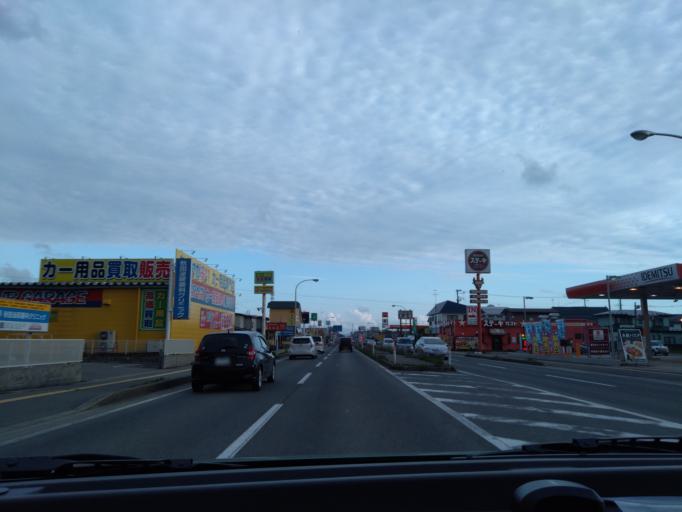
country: JP
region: Akita
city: Akita
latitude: 39.7232
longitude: 140.1482
